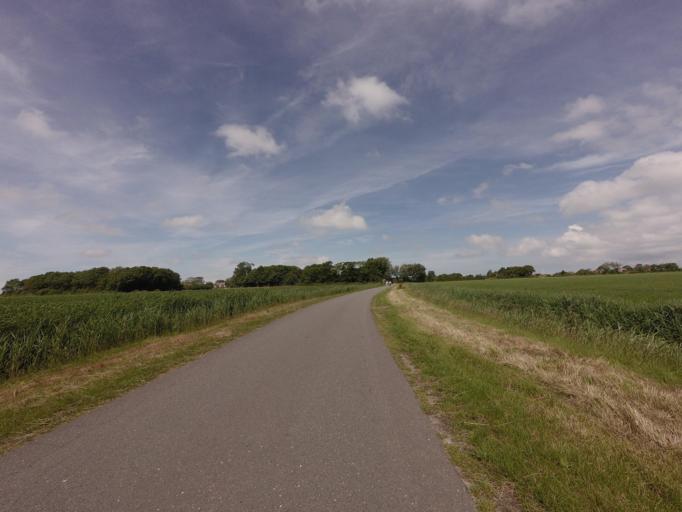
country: NL
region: North Holland
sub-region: Gemeente Texel
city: Den Burg
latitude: 53.0814
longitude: 4.8806
